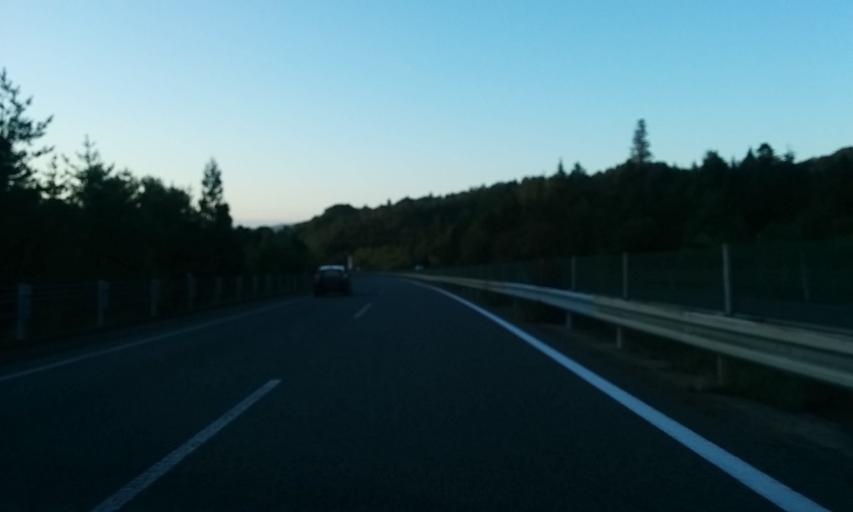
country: JP
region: Kyoto
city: Ayabe
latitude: 35.2353
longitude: 135.1887
